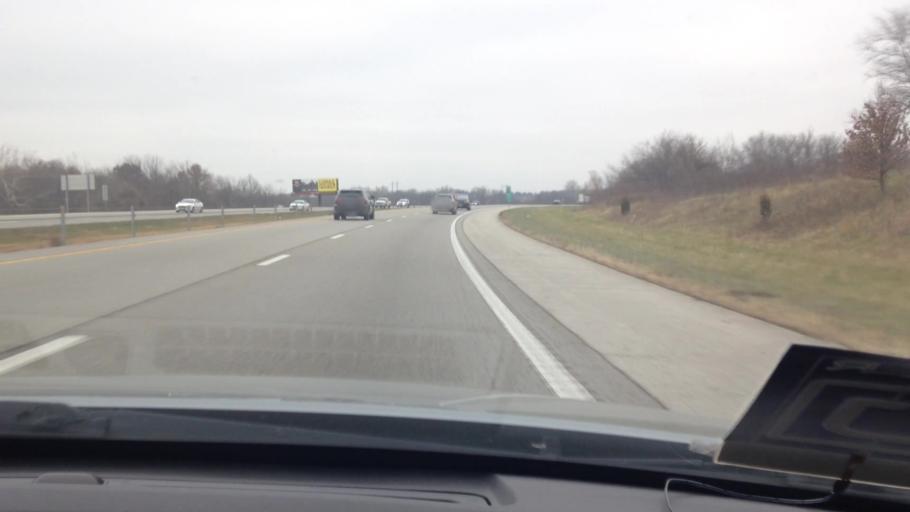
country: US
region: Missouri
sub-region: Cass County
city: Peculiar
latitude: 38.7622
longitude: -94.4886
